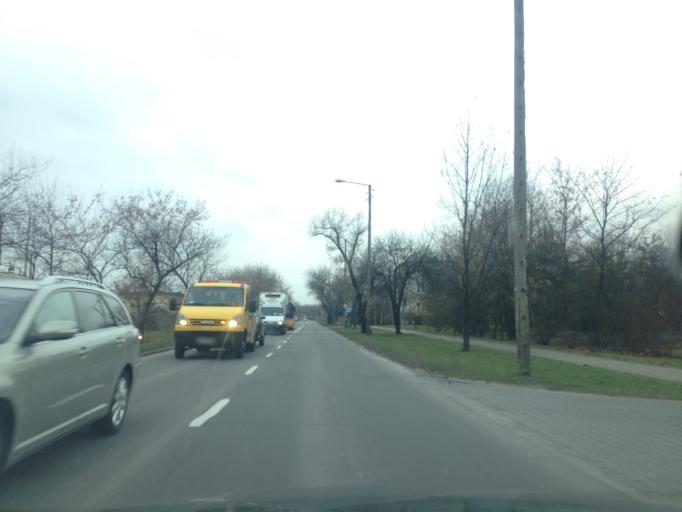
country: PL
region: Masovian Voivodeship
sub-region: Warszawa
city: Rembertow
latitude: 52.2568
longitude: 21.1757
